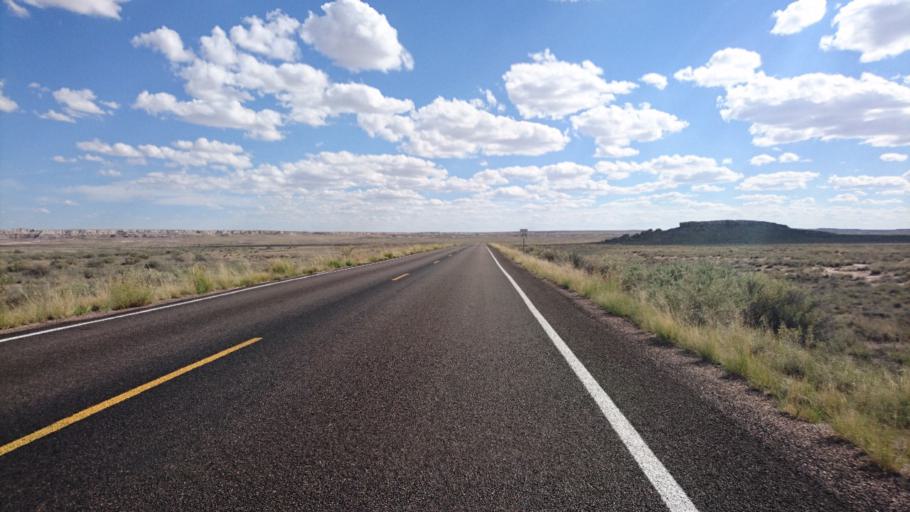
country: US
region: Arizona
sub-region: Navajo County
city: Holbrook
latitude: 34.8868
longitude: -109.8015
